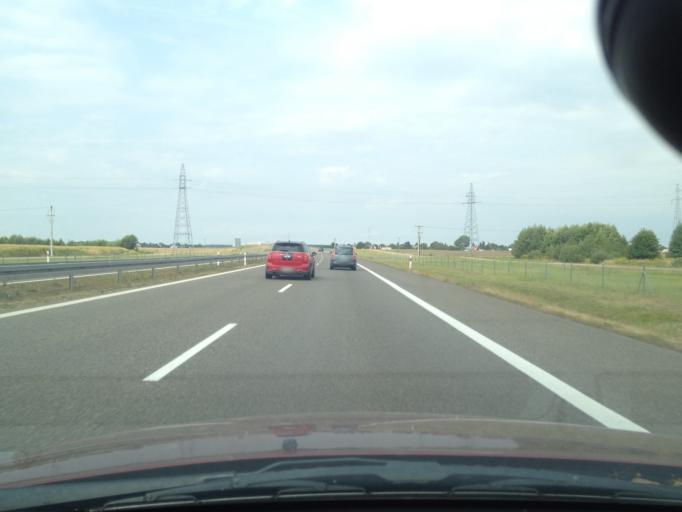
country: PL
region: West Pomeranian Voivodeship
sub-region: Powiat pyrzycki
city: Lipiany
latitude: 52.9439
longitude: 14.9697
